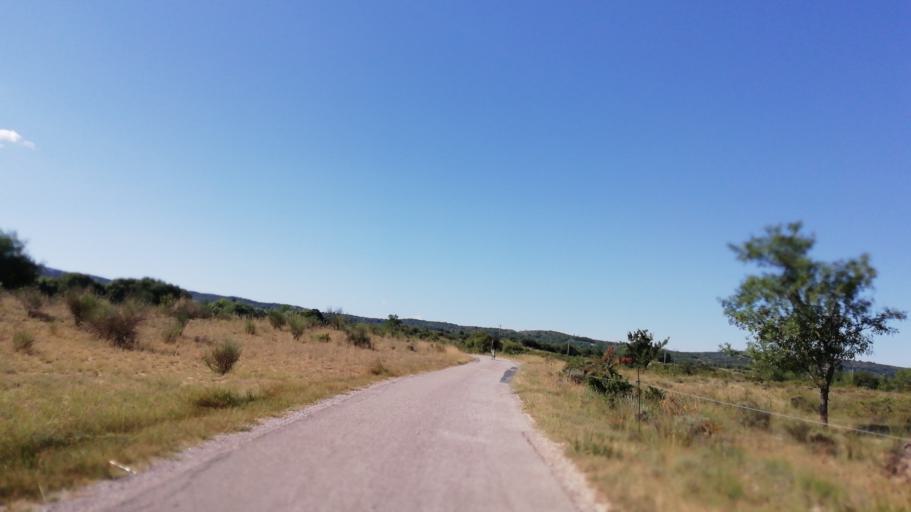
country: FR
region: Languedoc-Roussillon
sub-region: Departement de l'Herault
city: Saint-Martin-de-Londres
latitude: 43.7999
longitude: 3.7600
